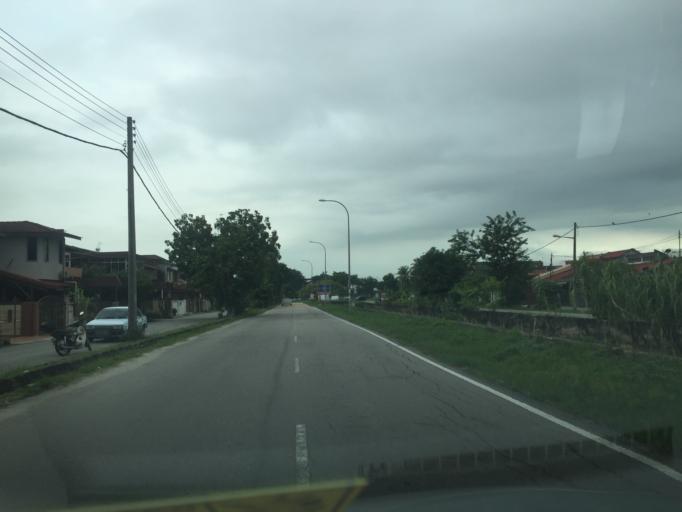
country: MY
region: Selangor
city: Klang
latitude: 3.0239
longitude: 101.4320
